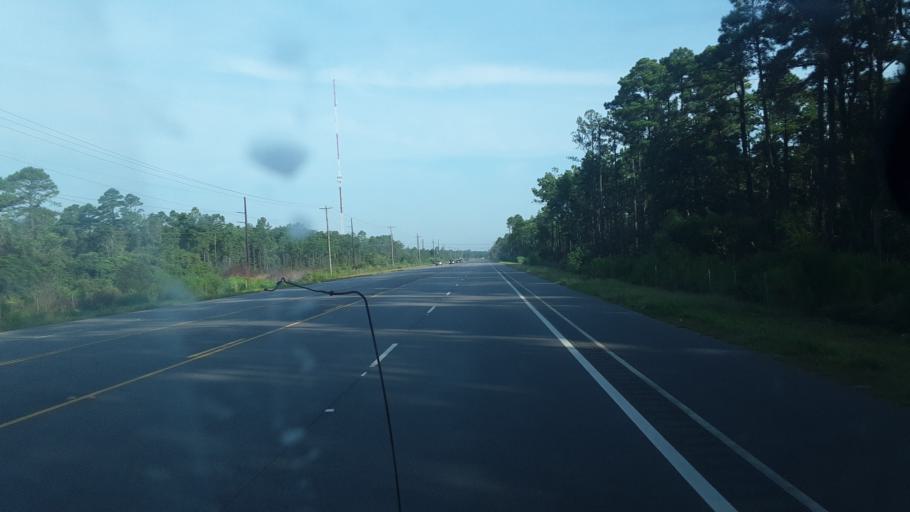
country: US
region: South Carolina
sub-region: Horry County
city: Myrtle Beach
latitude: 33.7792
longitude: -78.8736
